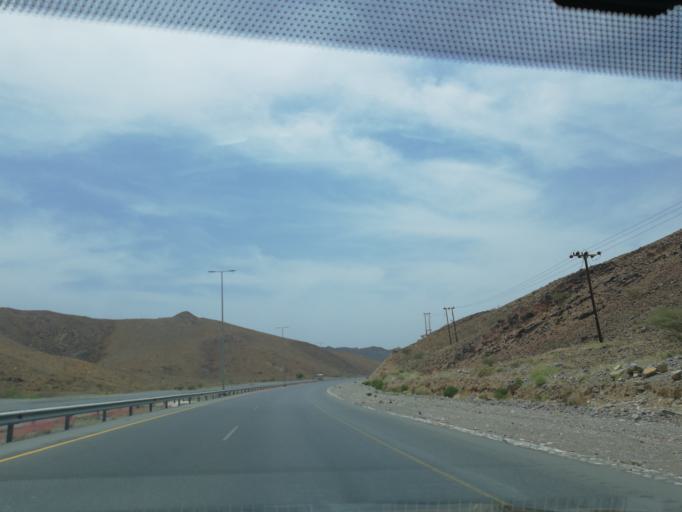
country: OM
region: Muhafazat ad Dakhiliyah
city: Izki
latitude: 22.8860
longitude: 57.7158
